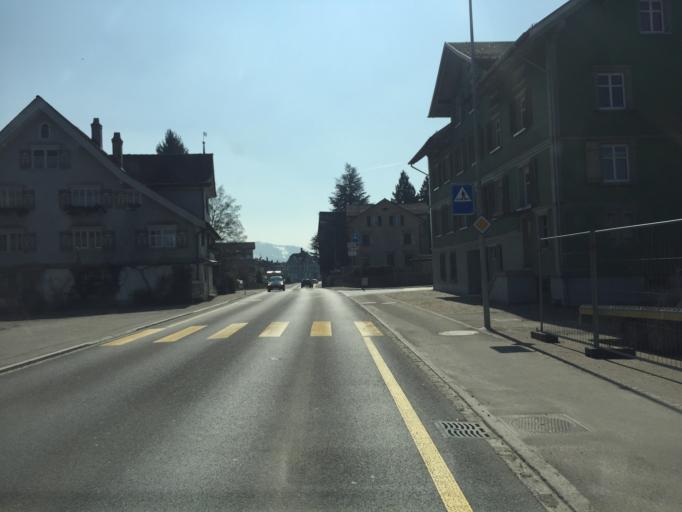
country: CH
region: Saint Gallen
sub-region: Wahlkreis Toggenburg
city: Buetschwil
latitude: 47.3630
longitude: 9.0734
